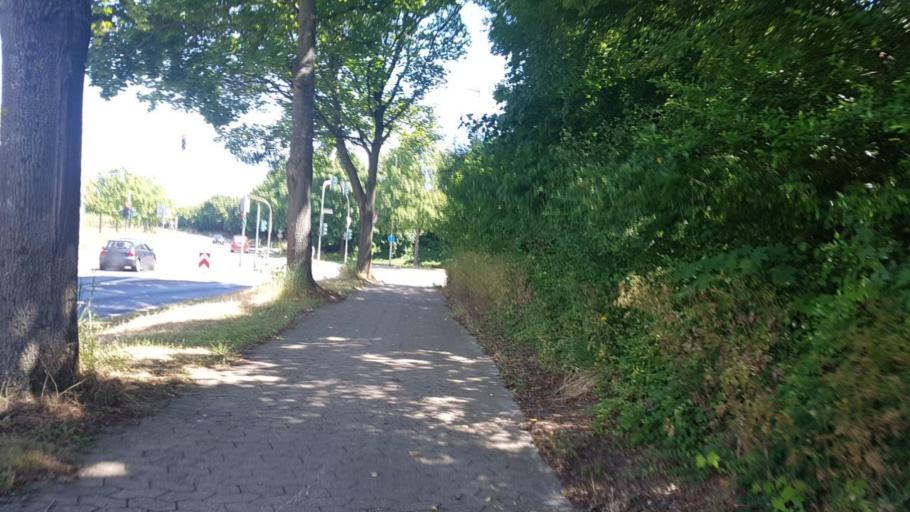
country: DE
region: North Rhine-Westphalia
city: Meckenheim
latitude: 50.6278
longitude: 7.0312
